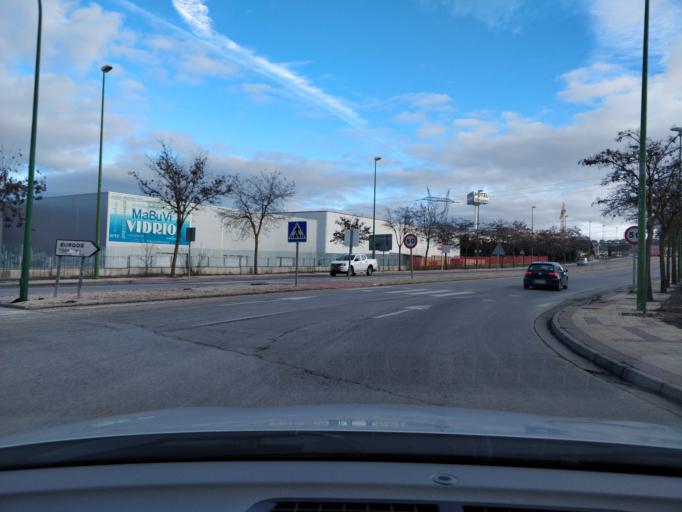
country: ES
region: Castille and Leon
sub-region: Provincia de Burgos
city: Burgos
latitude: 42.3660
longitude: -3.7143
